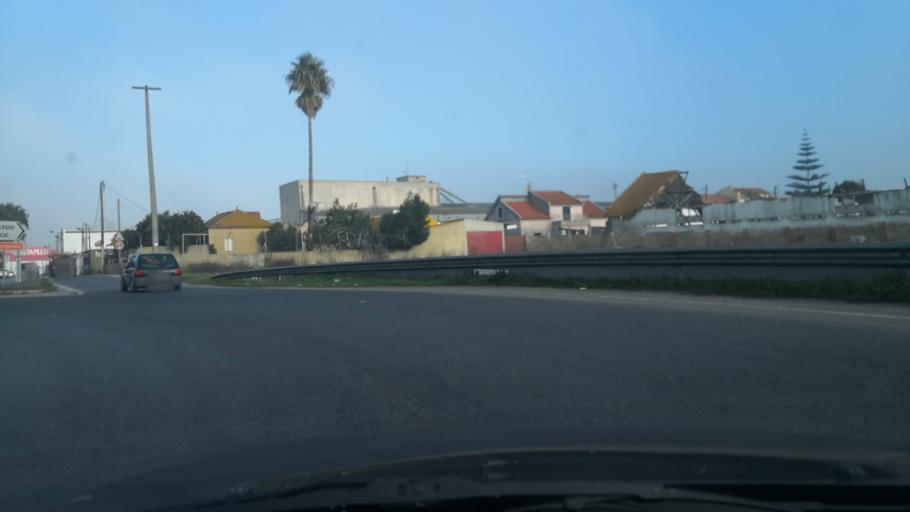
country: PT
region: Setubal
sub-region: Montijo
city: Montijo
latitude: 38.6865
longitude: -8.9439
